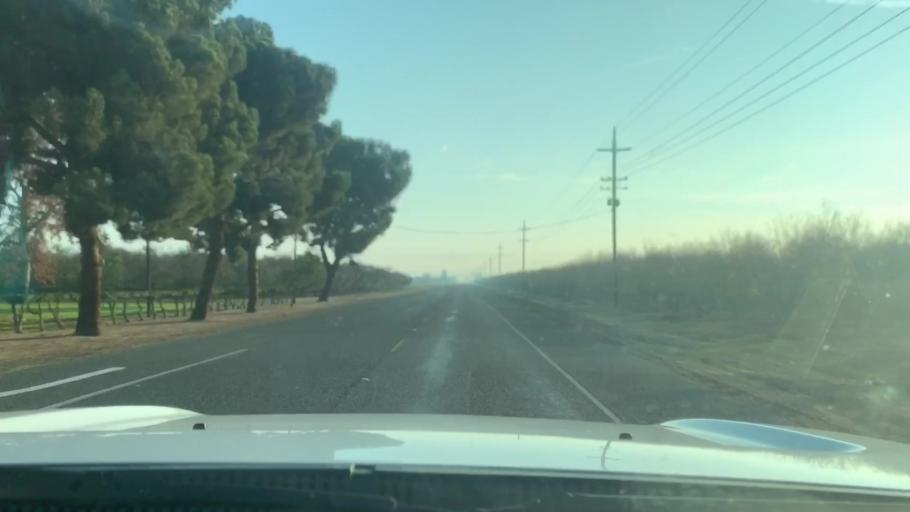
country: US
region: California
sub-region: Kern County
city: Wasco
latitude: 35.6015
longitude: -119.3834
